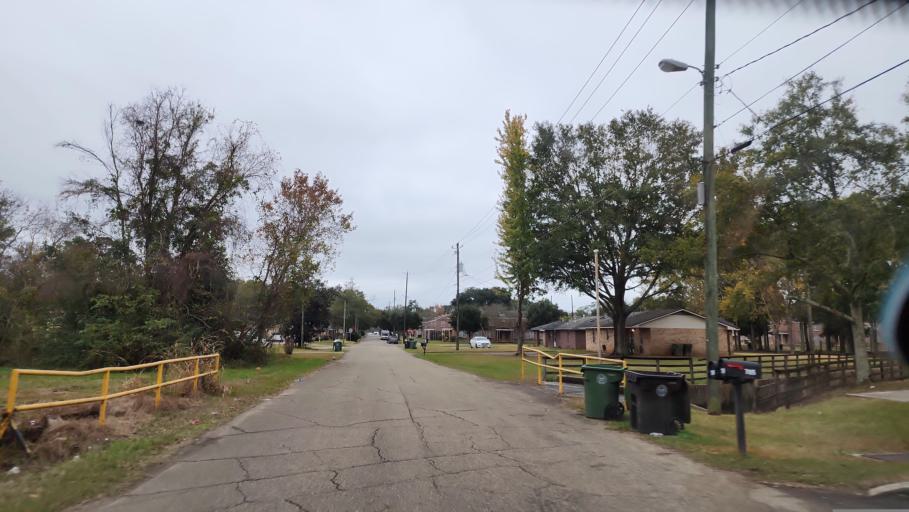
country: US
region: Mississippi
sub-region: Forrest County
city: Hattiesburg
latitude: 31.3168
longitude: -89.2947
